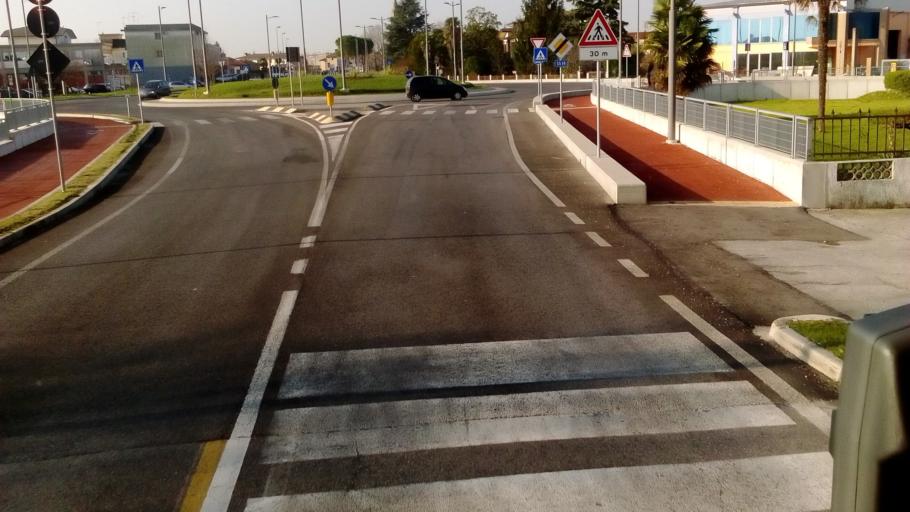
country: IT
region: Friuli Venezia Giulia
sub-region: Provincia di Udine
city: Muzzana del Turgnano
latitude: 45.8192
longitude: 13.1341
